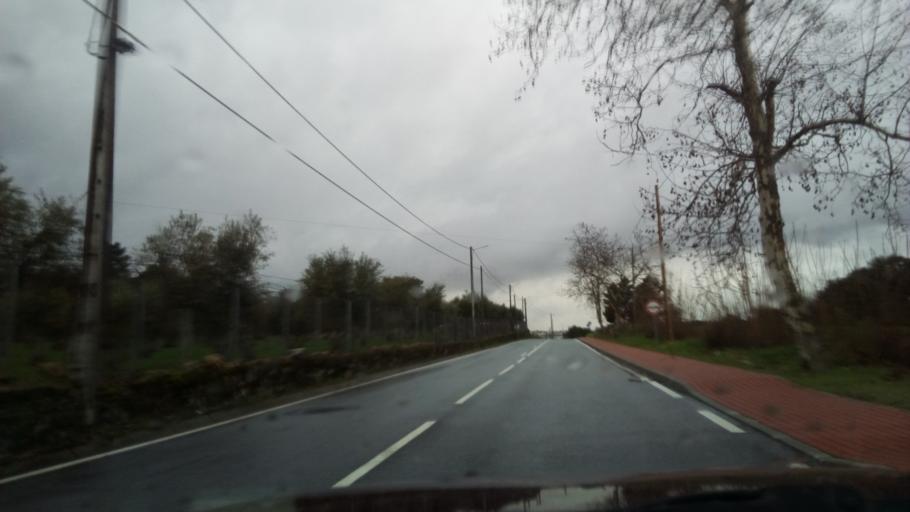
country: PT
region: Guarda
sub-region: Celorico da Beira
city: Celorico da Beira
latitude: 40.6396
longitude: -7.3652
